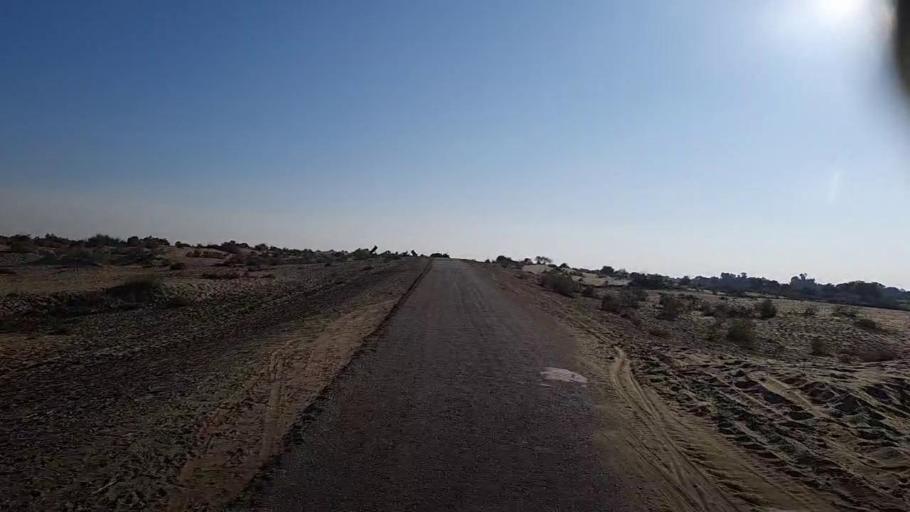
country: PK
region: Sindh
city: Khairpur
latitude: 27.9033
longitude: 69.7492
